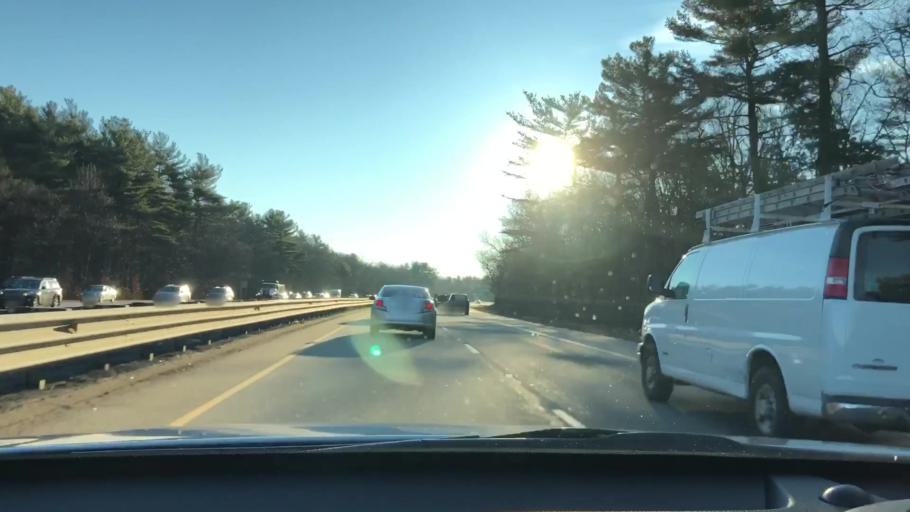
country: US
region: Massachusetts
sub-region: Norfolk County
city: Weymouth
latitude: 42.1831
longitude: -70.9228
